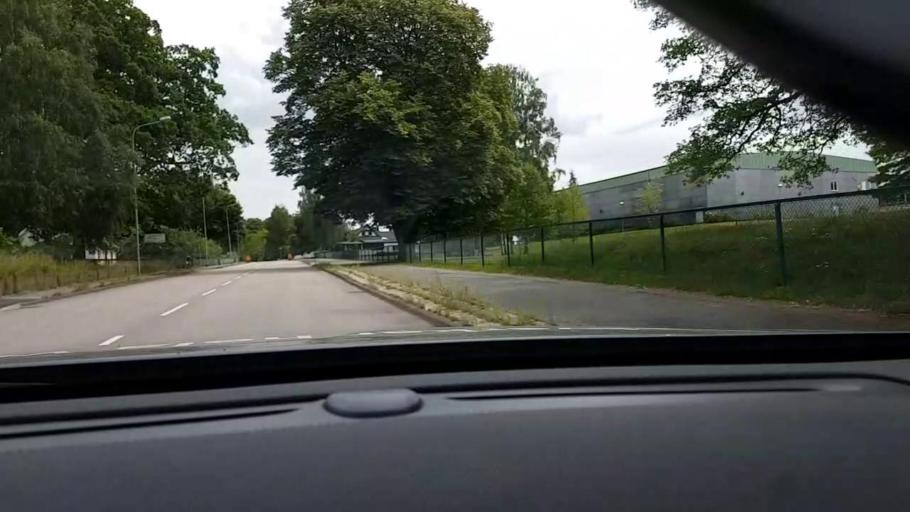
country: SE
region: Skane
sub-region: Hassleholms Kommun
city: Hassleholm
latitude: 56.1666
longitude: 13.7479
